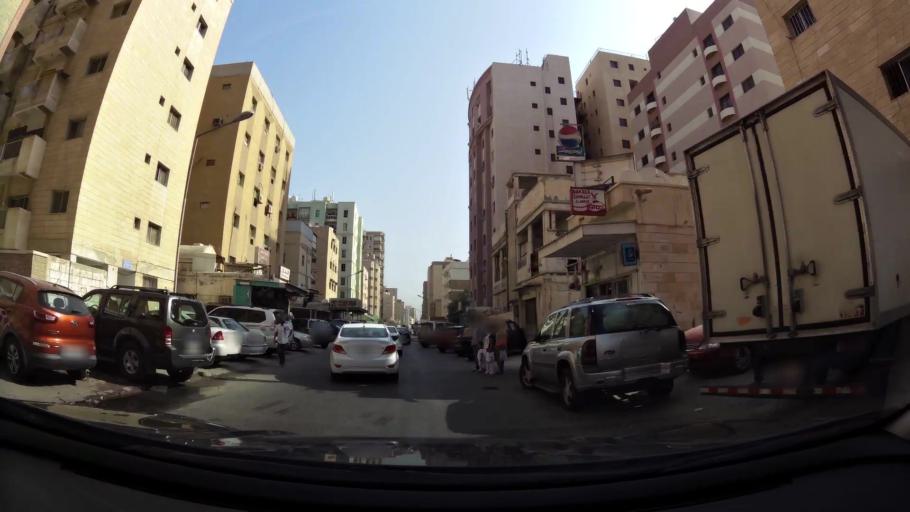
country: KW
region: Muhafazat Hawalli
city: Hawalli
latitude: 29.3276
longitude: 48.0132
